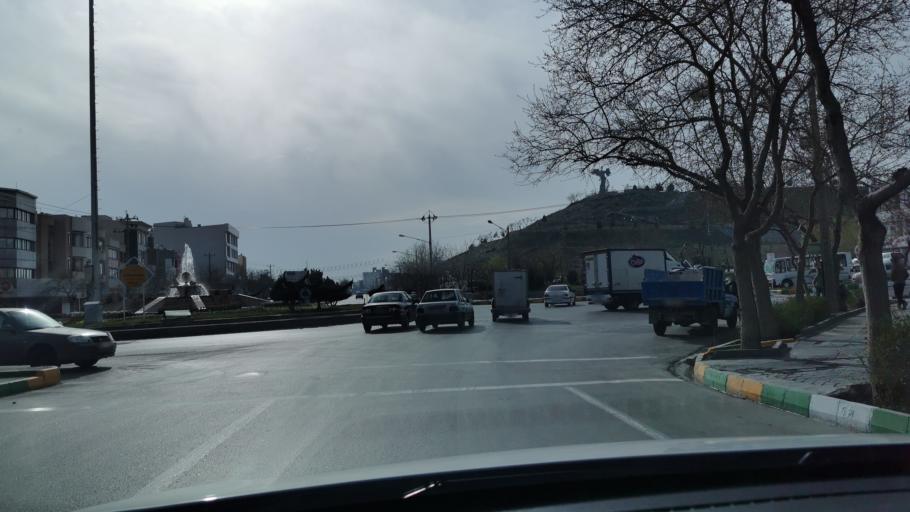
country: IR
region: Razavi Khorasan
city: Mashhad
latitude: 36.2962
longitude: 59.5289
